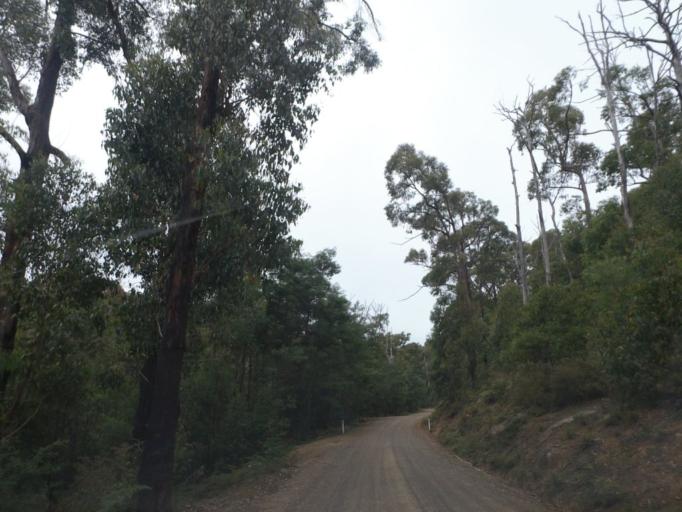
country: AU
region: Victoria
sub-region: Yarra Ranges
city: Healesville
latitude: -37.4235
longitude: 145.5825
